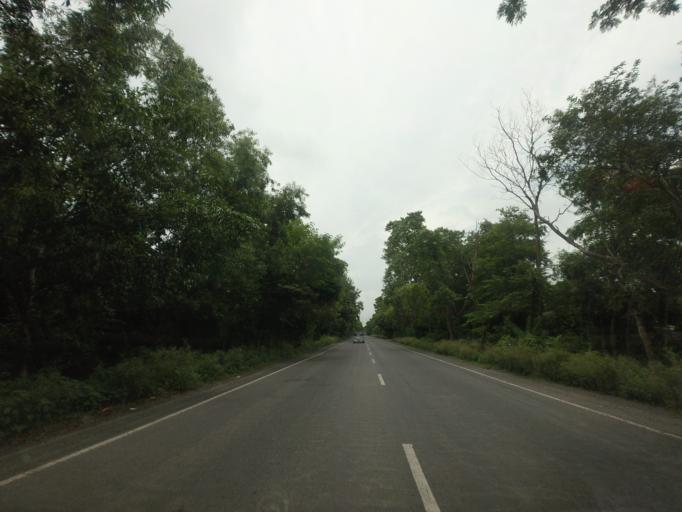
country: BD
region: Khulna
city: Kalia
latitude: 23.2812
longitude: 89.7979
